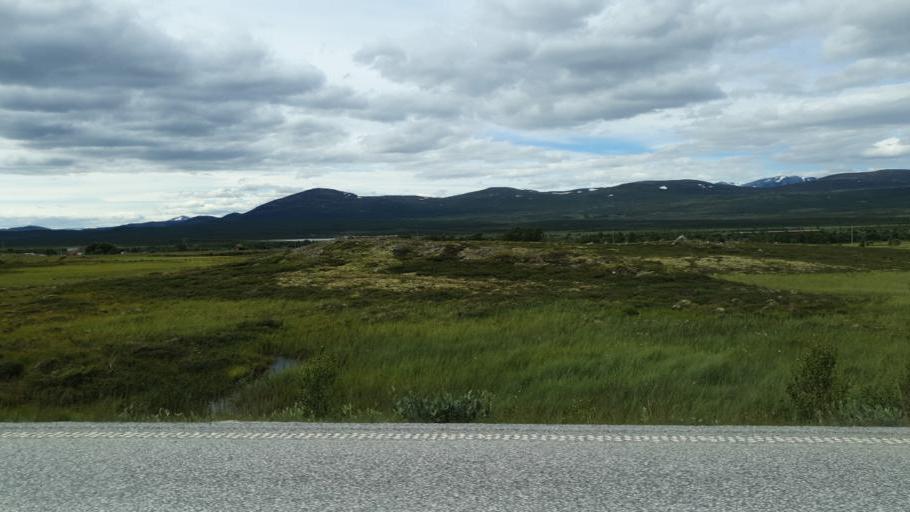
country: NO
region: Oppland
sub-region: Dovre
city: Dovre
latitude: 62.1151
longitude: 9.2917
